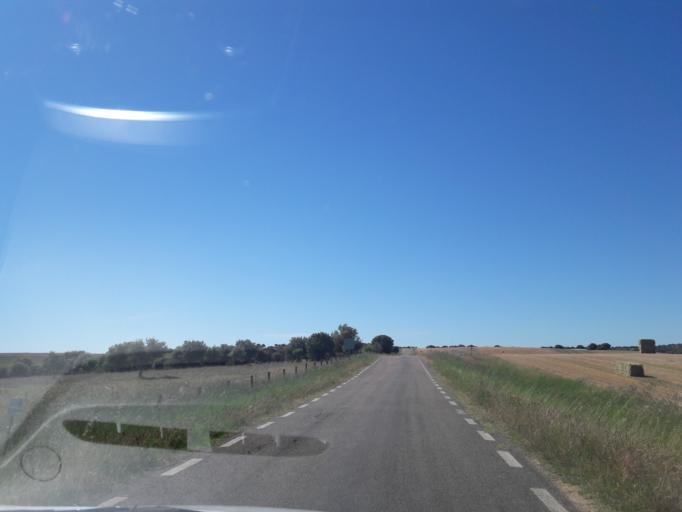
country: ES
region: Castille and Leon
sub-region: Provincia de Salamanca
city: Zarapicos
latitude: 41.0331
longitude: -5.8388
